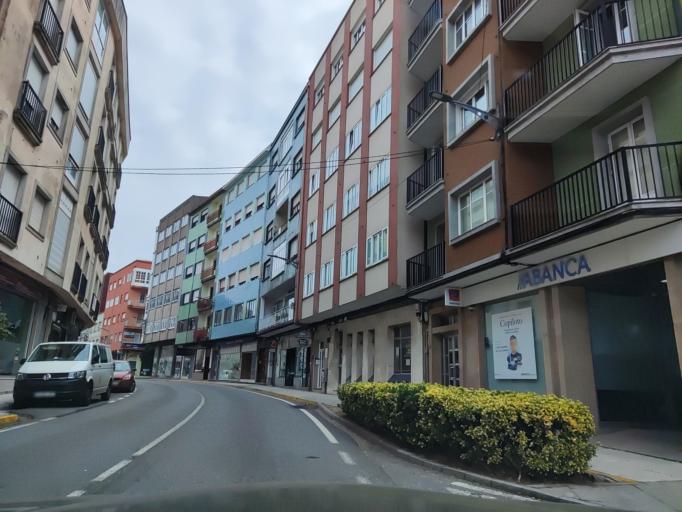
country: ES
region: Galicia
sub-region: Provincia da Coruna
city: Boiro
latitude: 42.6478
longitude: -8.8822
